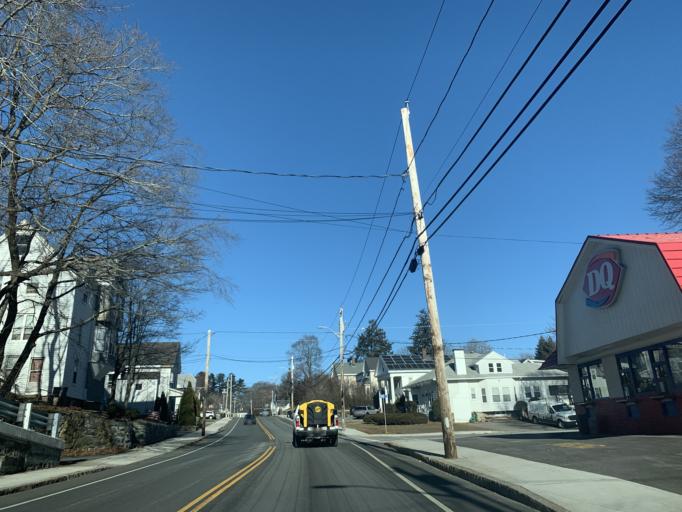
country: US
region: Massachusetts
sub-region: Middlesex County
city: Marlborough
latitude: 42.3490
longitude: -71.5419
